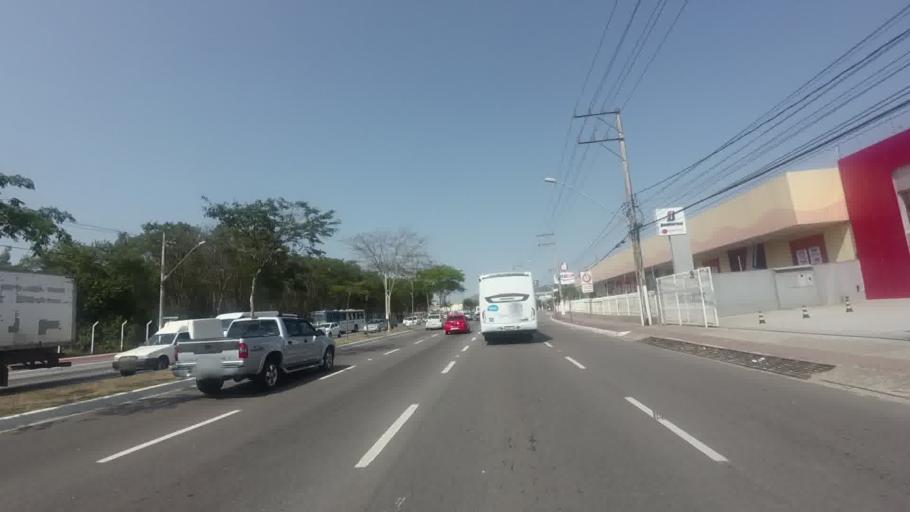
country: BR
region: Espirito Santo
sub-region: Vila Velha
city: Vila Velha
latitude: -20.2634
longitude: -40.2953
